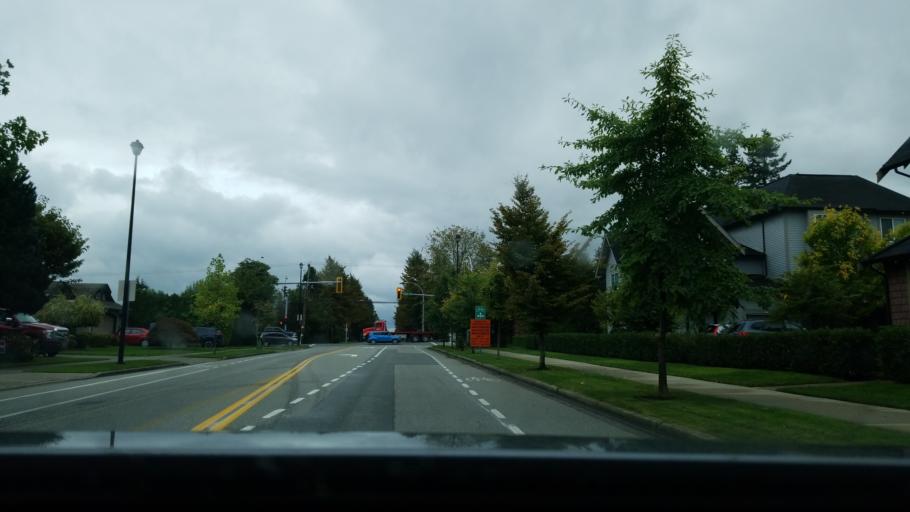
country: CA
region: British Columbia
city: Langley
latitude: 49.1198
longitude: -122.7018
